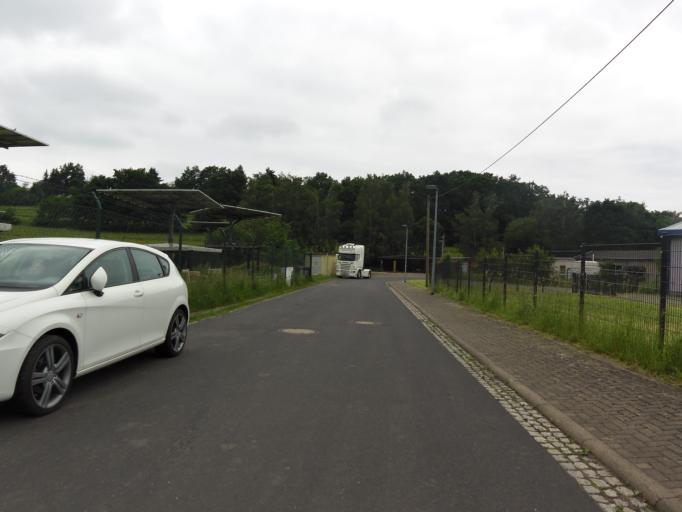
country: DE
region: Thuringia
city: Tabarz
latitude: 50.8837
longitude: 10.5101
